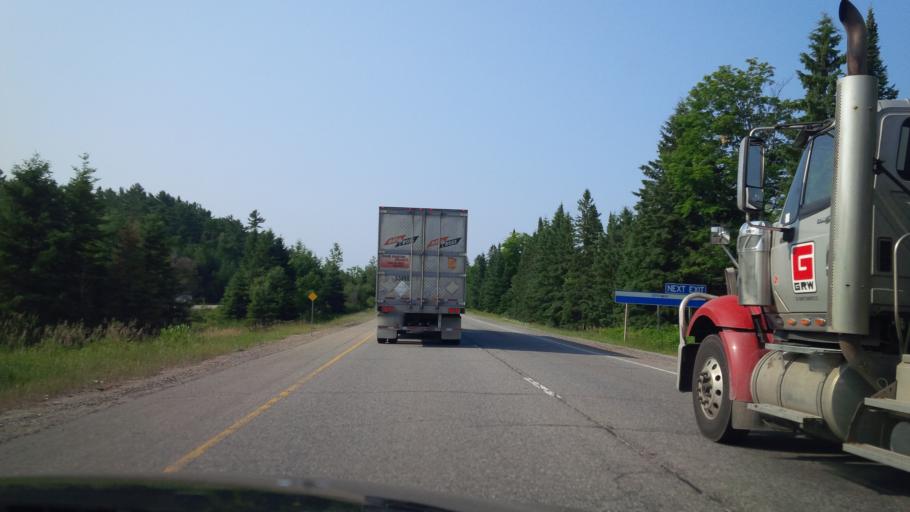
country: CA
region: Ontario
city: Huntsville
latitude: 45.2488
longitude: -79.2981
